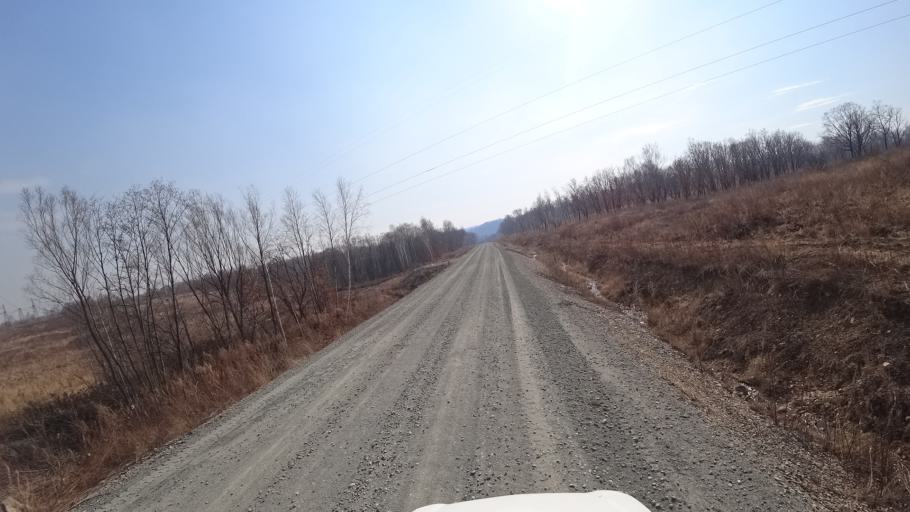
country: RU
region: Amur
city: Novobureyskiy
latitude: 49.8026
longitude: 129.9615
